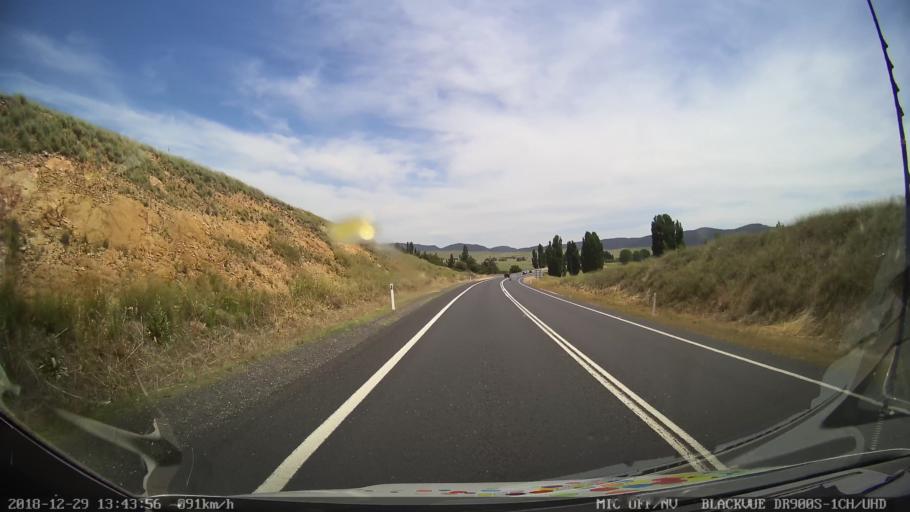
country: AU
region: New South Wales
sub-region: Cooma-Monaro
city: Cooma
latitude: -36.0795
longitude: 149.1591
